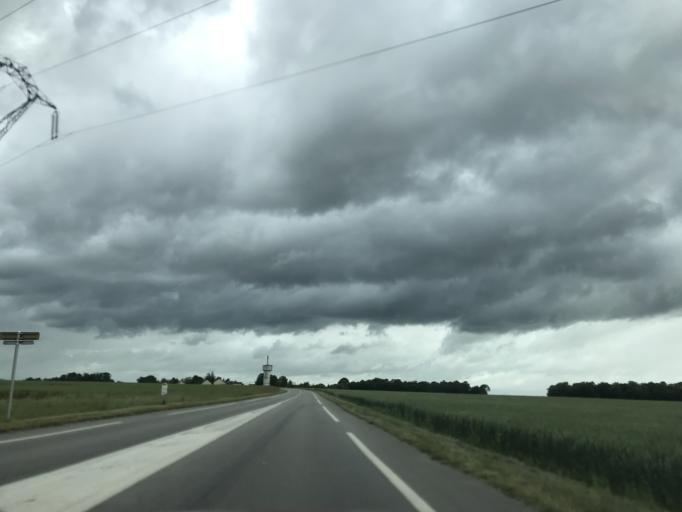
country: FR
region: Haute-Normandie
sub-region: Departement de l'Eure
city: La Couture-Boussey
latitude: 48.8948
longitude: 1.4206
